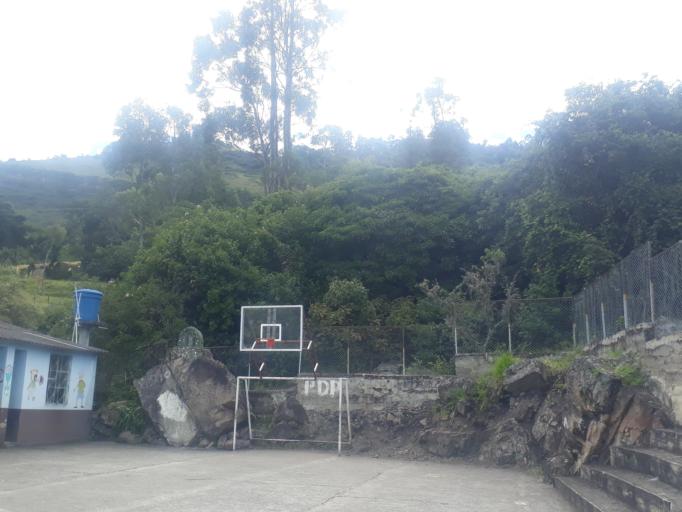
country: CO
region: Boyaca
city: El Espino
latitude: 6.5059
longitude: -72.5152
